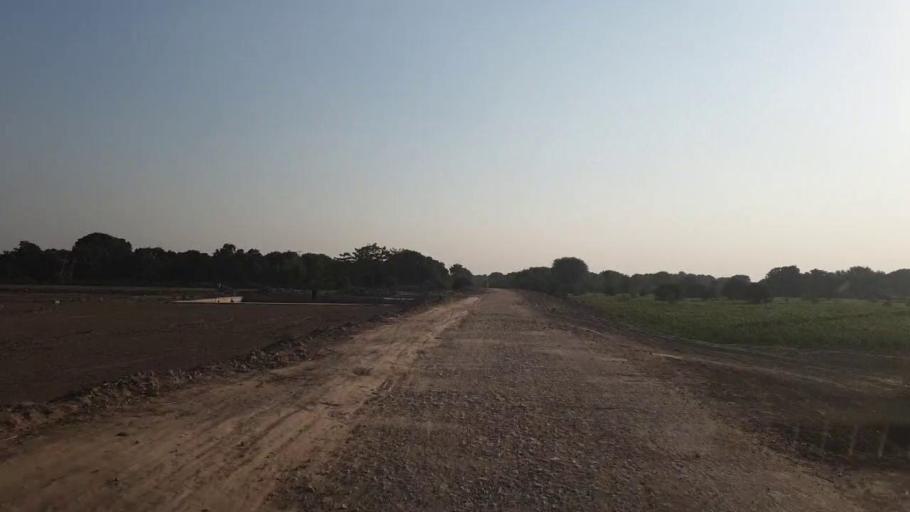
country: PK
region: Sindh
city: Mirpur Khas
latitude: 25.4188
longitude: 68.9065
